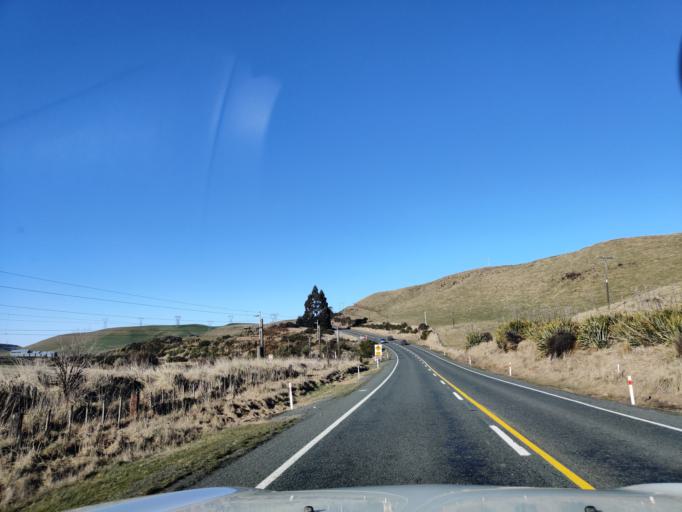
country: NZ
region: Manawatu-Wanganui
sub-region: Ruapehu District
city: Waiouru
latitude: -39.5226
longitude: 175.6846
